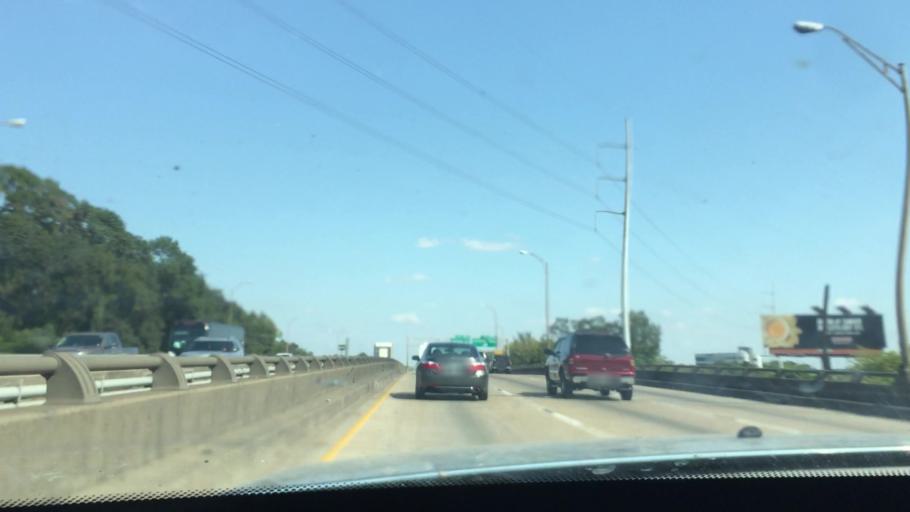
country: US
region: Louisiana
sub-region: East Baton Rouge Parish
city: Baton Rouge
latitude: 30.4247
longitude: -91.1561
